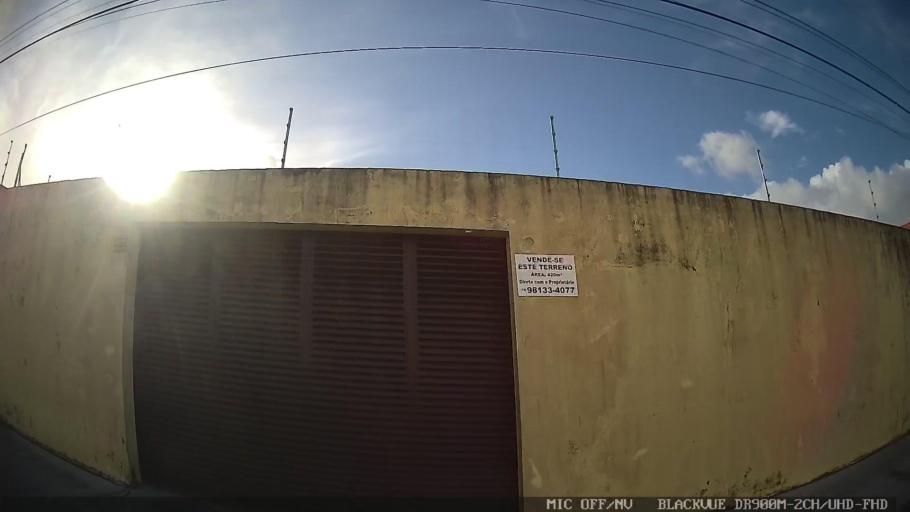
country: BR
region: Sao Paulo
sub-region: Itanhaem
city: Itanhaem
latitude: -24.2094
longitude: -46.8385
